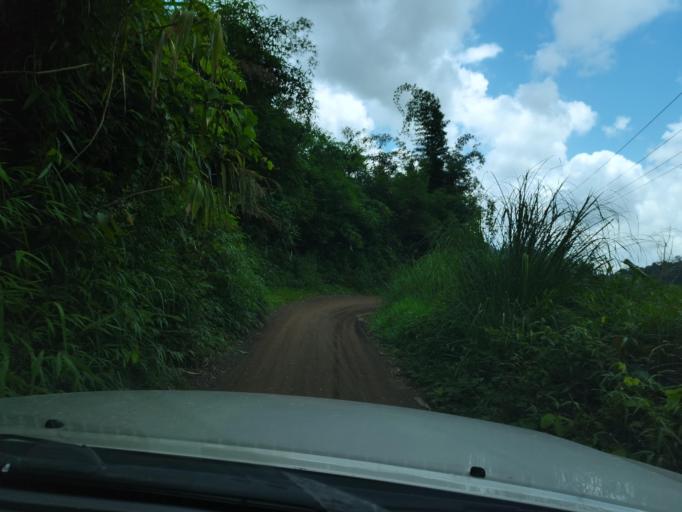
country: LA
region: Loungnamtha
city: Muang Long
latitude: 20.7584
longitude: 101.0168
